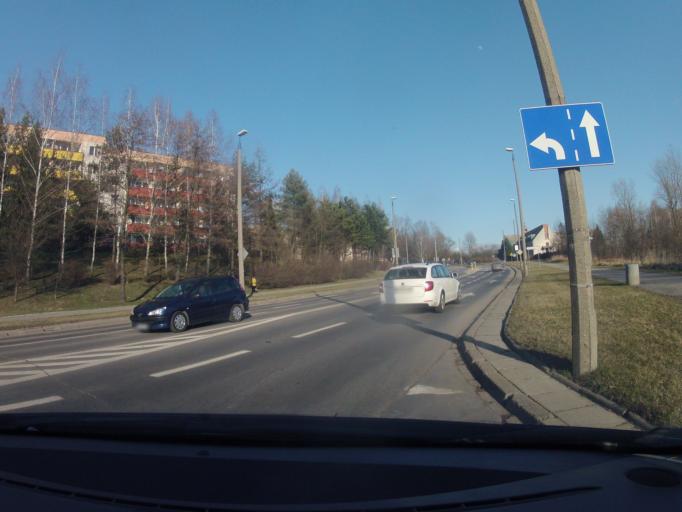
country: PL
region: Lesser Poland Voivodeship
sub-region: Powiat krakowski
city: Wrzasowice
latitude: 50.0046
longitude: 19.9617
